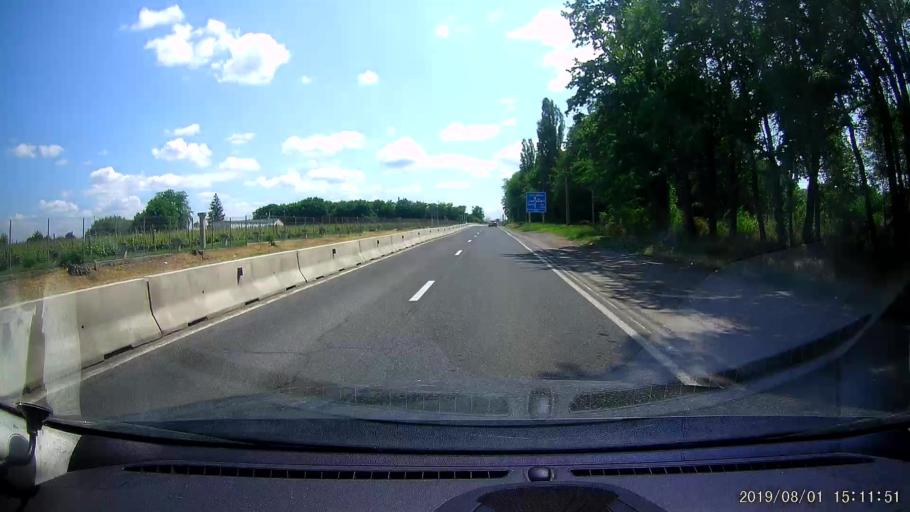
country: RO
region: Braila
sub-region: Comuna Chiscani
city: Chiscani
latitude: 45.2133
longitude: 27.9201
